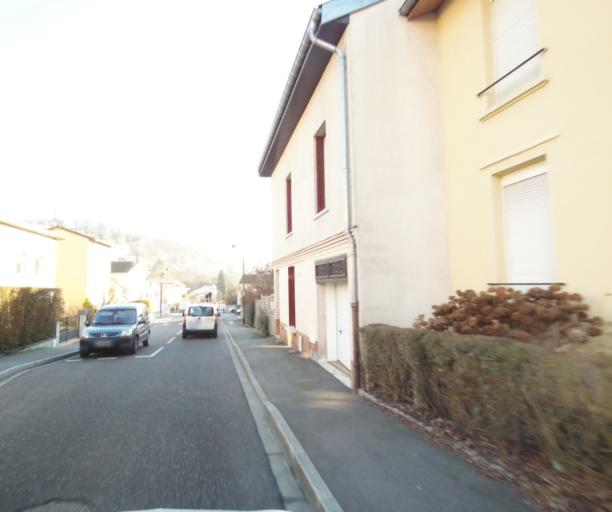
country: FR
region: Lorraine
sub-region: Departement de Meurthe-et-Moselle
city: Laxou
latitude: 48.6865
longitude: 6.1365
